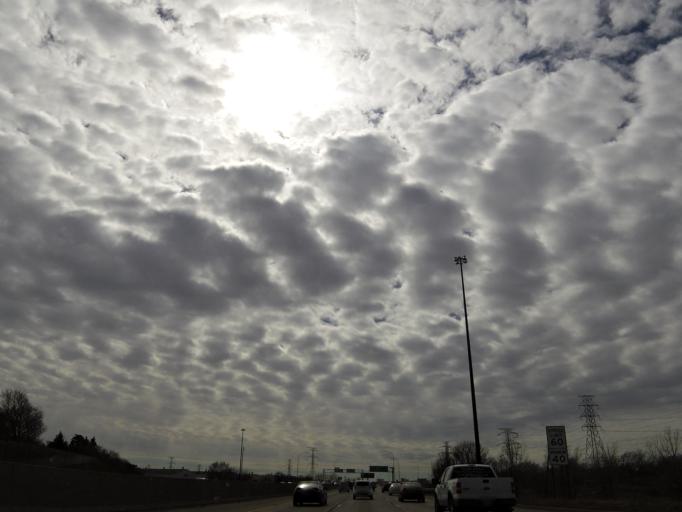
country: US
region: Minnesota
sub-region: Ramsey County
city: Lauderdale
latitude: 45.0090
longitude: -93.2031
